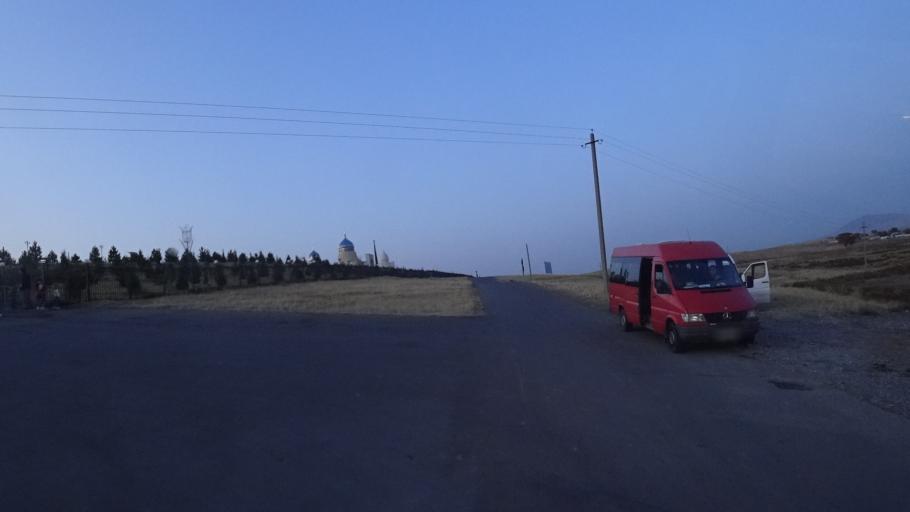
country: KZ
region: Ongtustik Qazaqstan
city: Qazyqurt
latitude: 41.8746
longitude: 69.4279
